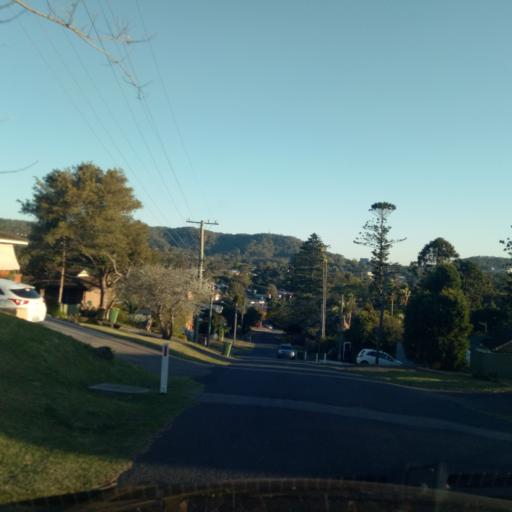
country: AU
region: New South Wales
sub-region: Gosford Shire
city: Narara
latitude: -33.4009
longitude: 151.3505
